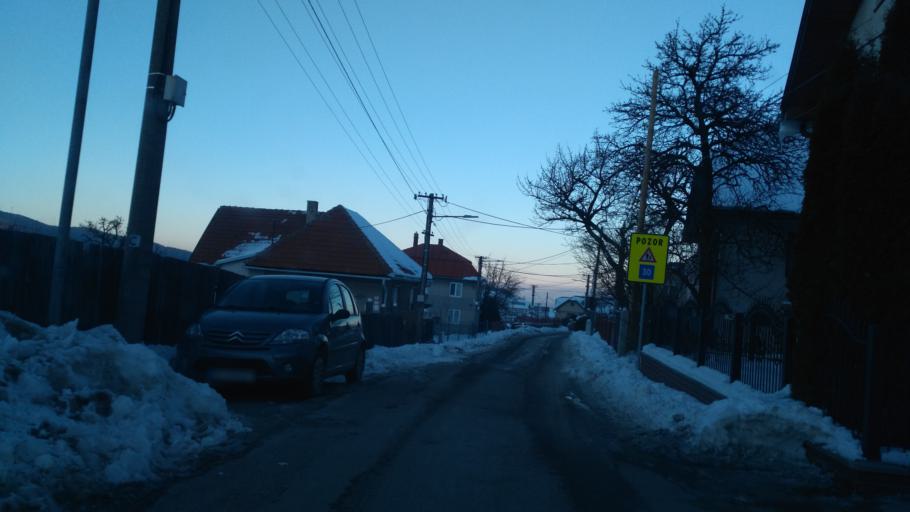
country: SK
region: Kosicky
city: Kosice
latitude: 48.7720
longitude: 21.2060
